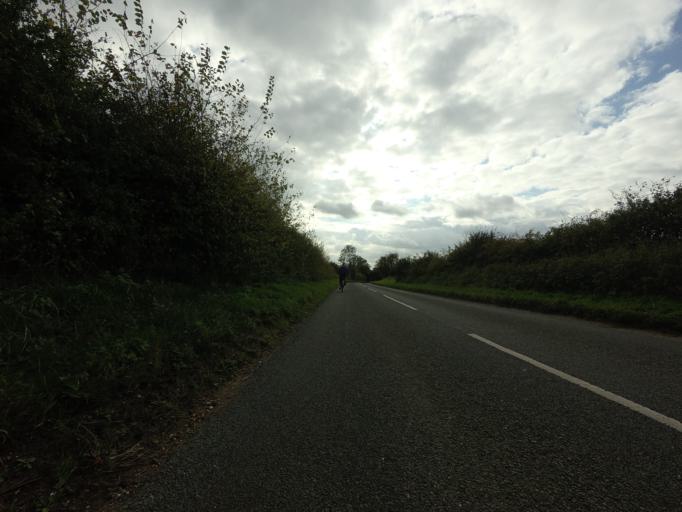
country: GB
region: England
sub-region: Norfolk
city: Snettisham
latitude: 52.8814
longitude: 0.5190
